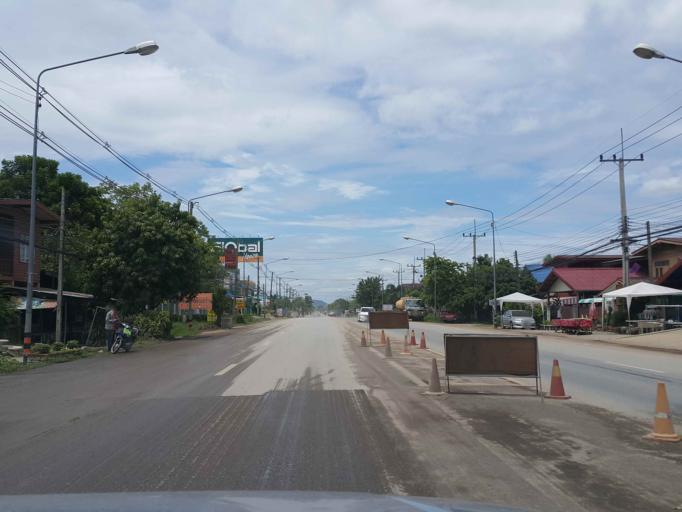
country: TH
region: Sukhothai
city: Ban Na
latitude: 17.0120
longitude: 99.7724
